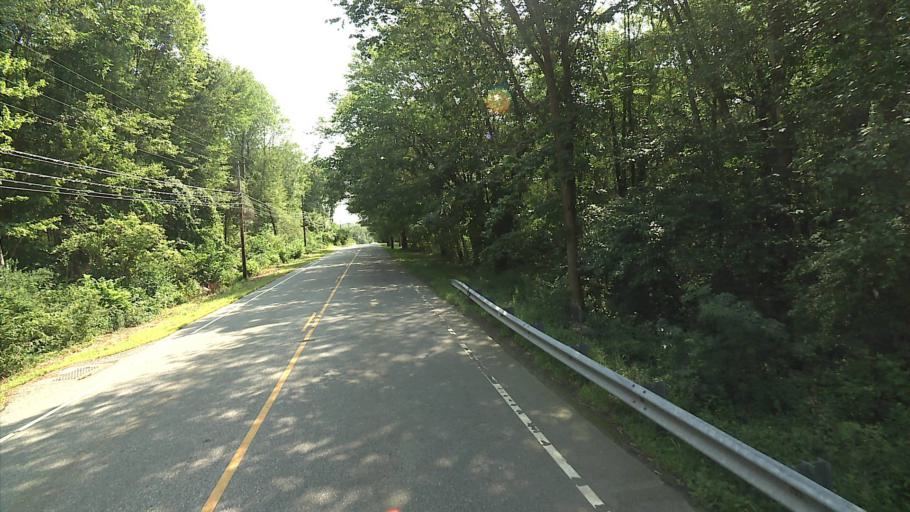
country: US
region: Connecticut
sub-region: New London County
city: Colchester
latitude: 41.5731
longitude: -72.2180
